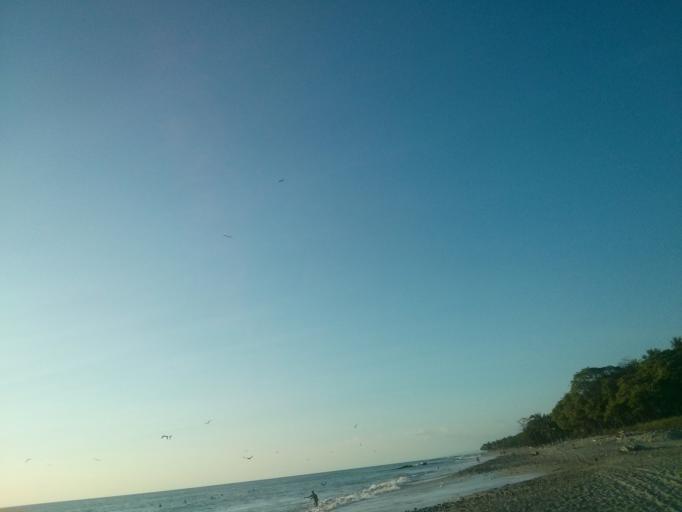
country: CR
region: Guanacaste
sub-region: Canton de Nandayure
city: Bejuco
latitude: 9.6291
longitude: -85.1549
